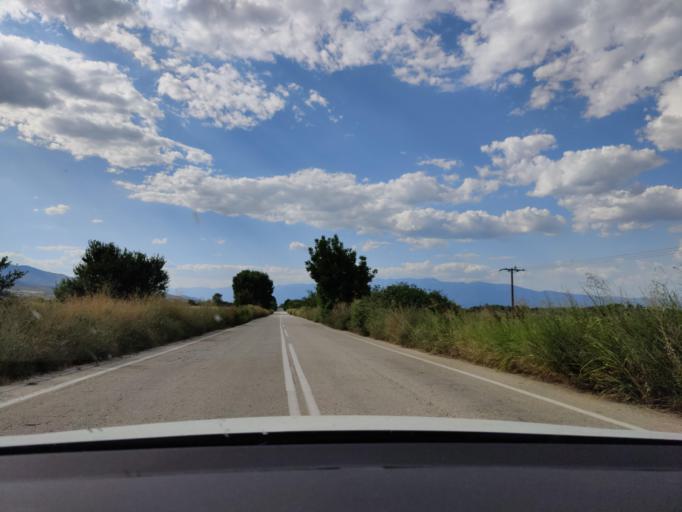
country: GR
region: Central Macedonia
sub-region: Nomos Serron
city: Strymoniko
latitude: 41.0792
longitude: 23.2930
